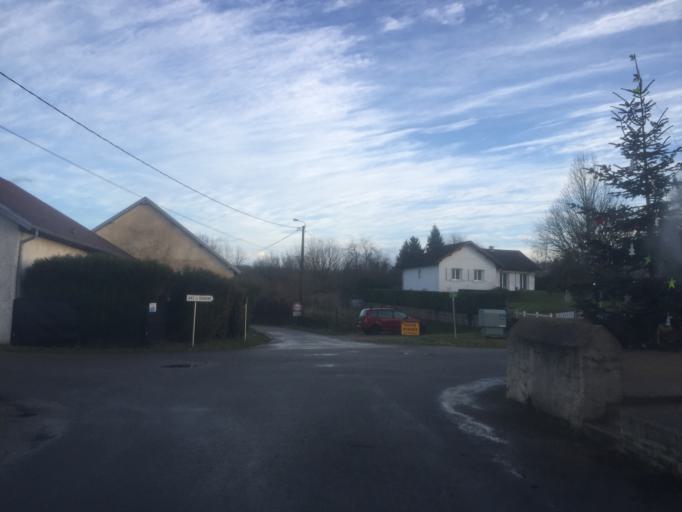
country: FR
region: Franche-Comte
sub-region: Departement du Jura
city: Dampierre
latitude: 47.1242
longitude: 5.7114
